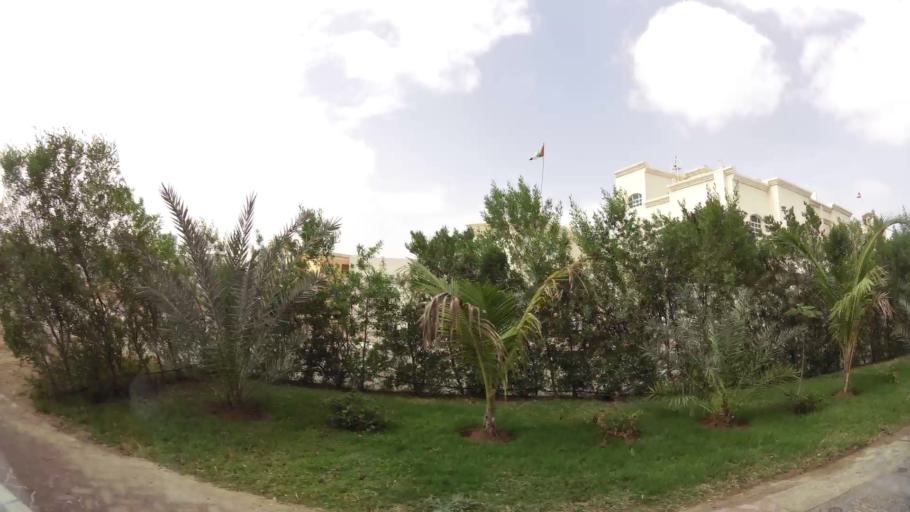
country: AE
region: Abu Dhabi
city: Abu Dhabi
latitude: 24.4026
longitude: 54.5221
